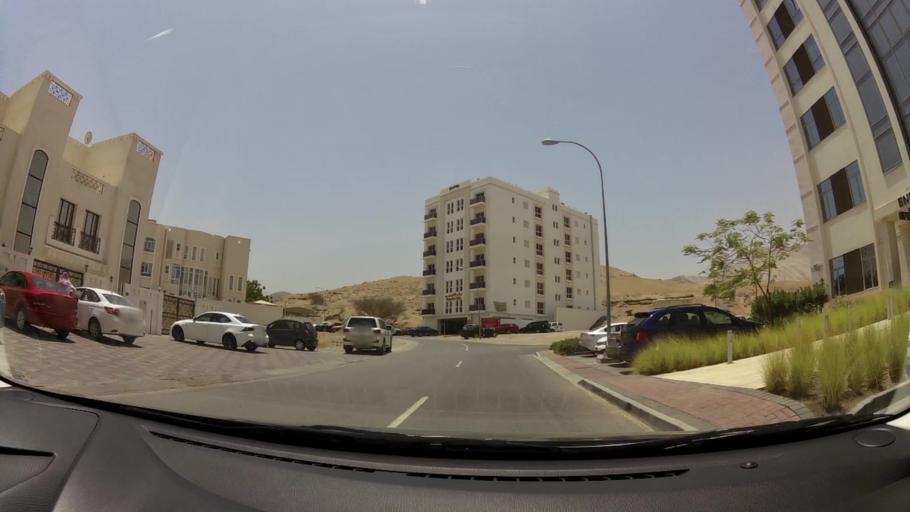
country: OM
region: Muhafazat Masqat
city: Bawshar
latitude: 23.5749
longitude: 58.4173
